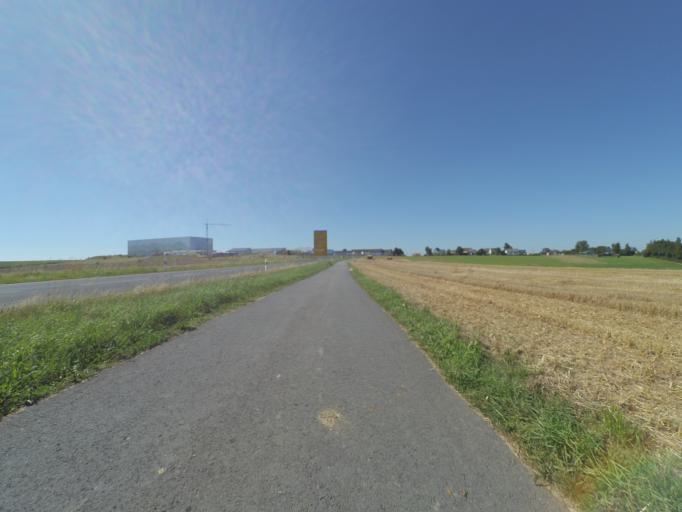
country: DE
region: Rheinland-Pfalz
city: Lutzerath
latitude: 50.1203
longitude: 7.0091
